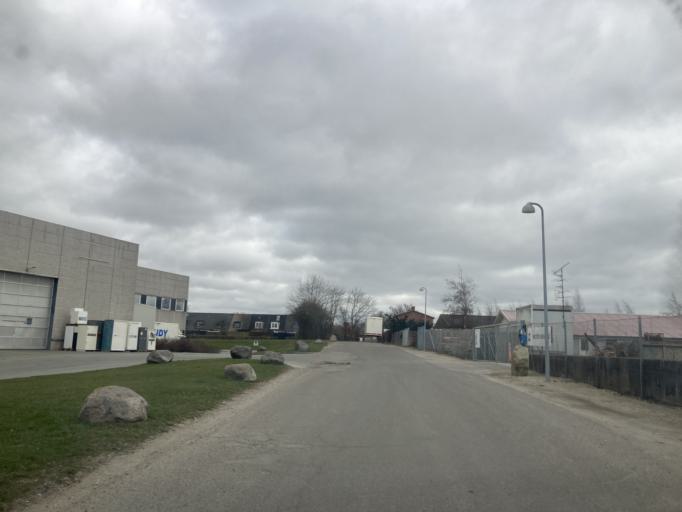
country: DK
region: Capital Region
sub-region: Hoje-Taastrup Kommune
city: Taastrup
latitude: 55.6606
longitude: 12.3036
